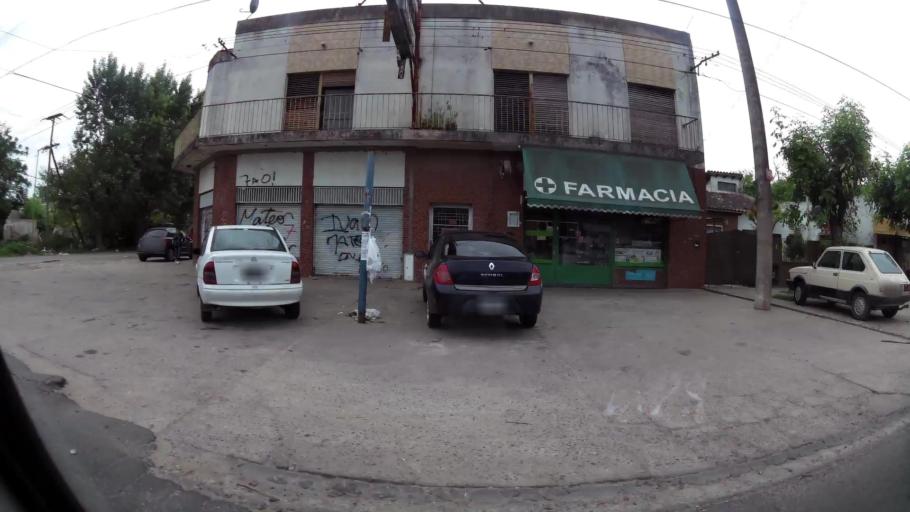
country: AR
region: Buenos Aires
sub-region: Partido de La Plata
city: La Plata
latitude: -34.9249
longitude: -58.0057
